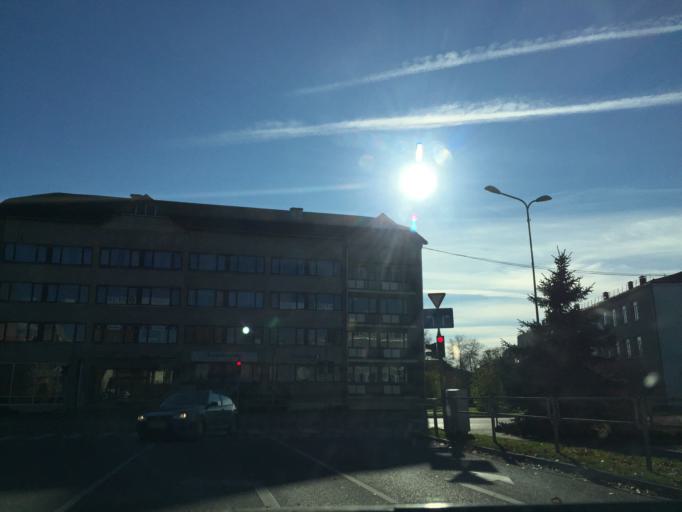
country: LV
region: Aizkraukles Rajons
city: Aizkraukle
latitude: 56.6010
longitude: 25.2549
